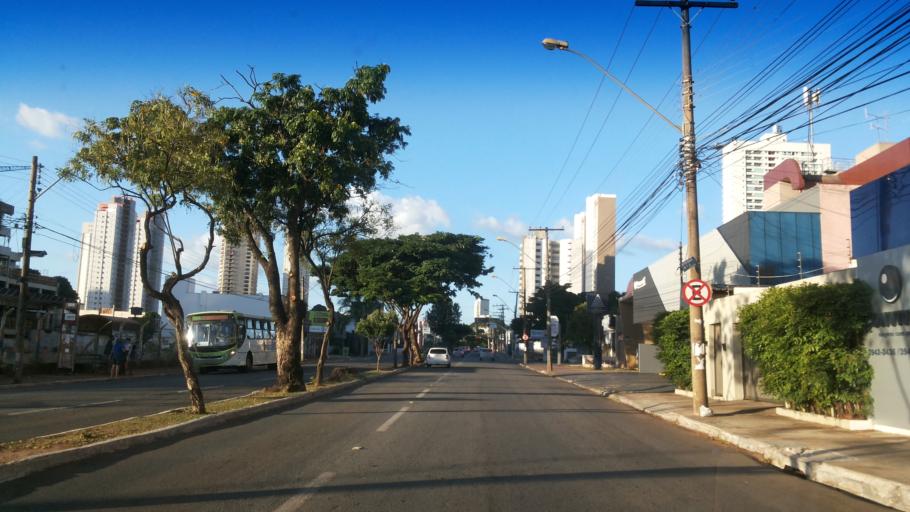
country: BR
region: Goias
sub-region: Goiania
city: Goiania
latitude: -16.7003
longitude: -49.2695
